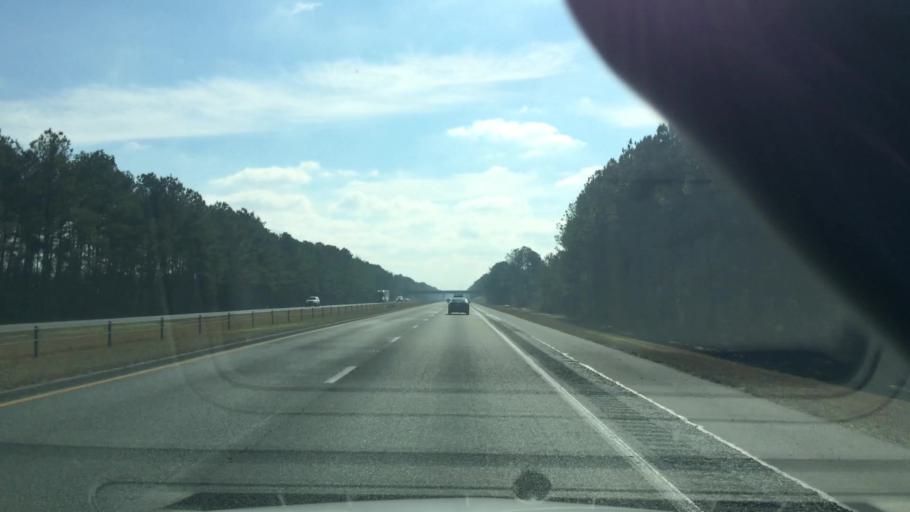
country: US
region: North Carolina
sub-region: Duplin County
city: Wallace
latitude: 34.7380
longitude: -77.9447
